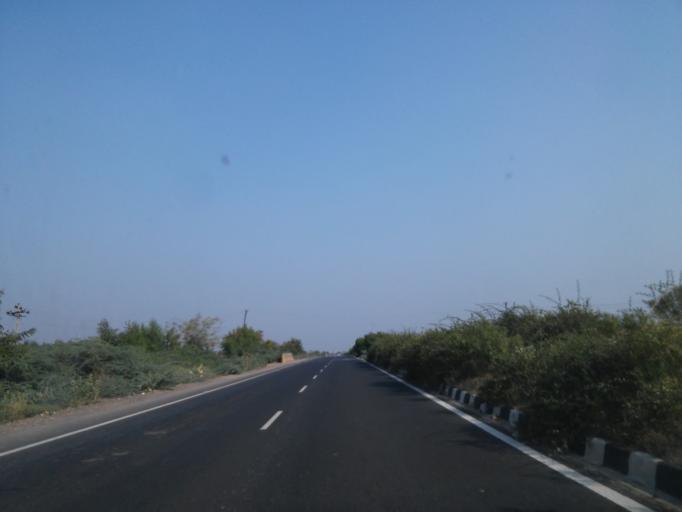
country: IN
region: Gujarat
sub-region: Surendranagar
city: Halvad
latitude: 23.0052
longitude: 71.1190
